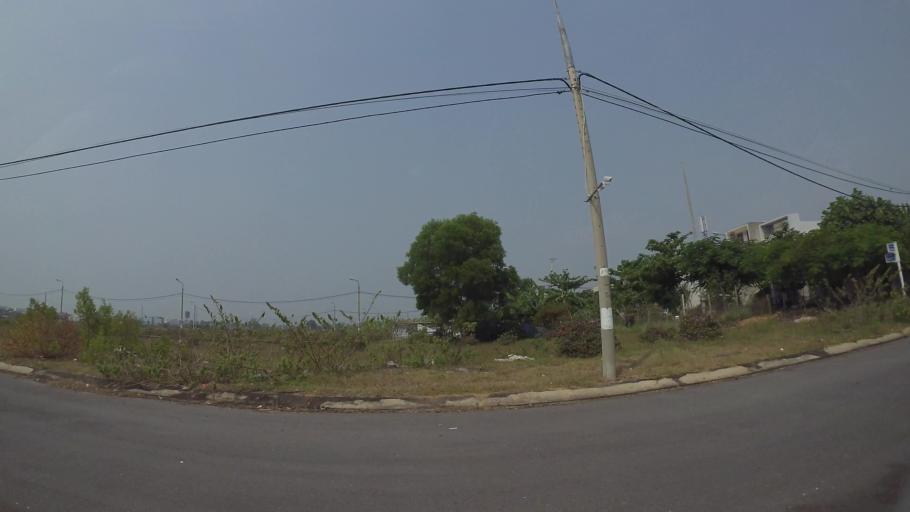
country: VN
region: Da Nang
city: Cam Le
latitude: 15.9750
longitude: 108.2145
